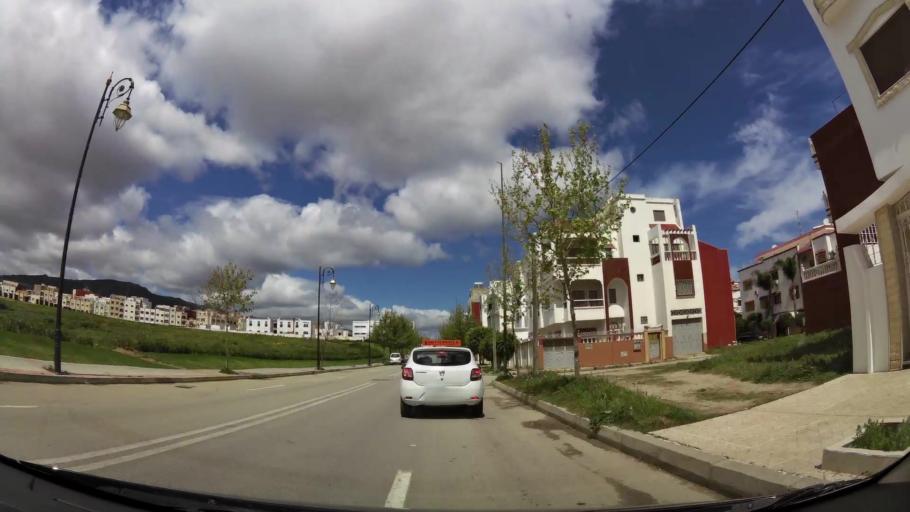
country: MA
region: Tanger-Tetouan
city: Tetouan
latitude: 35.5832
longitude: -5.3366
